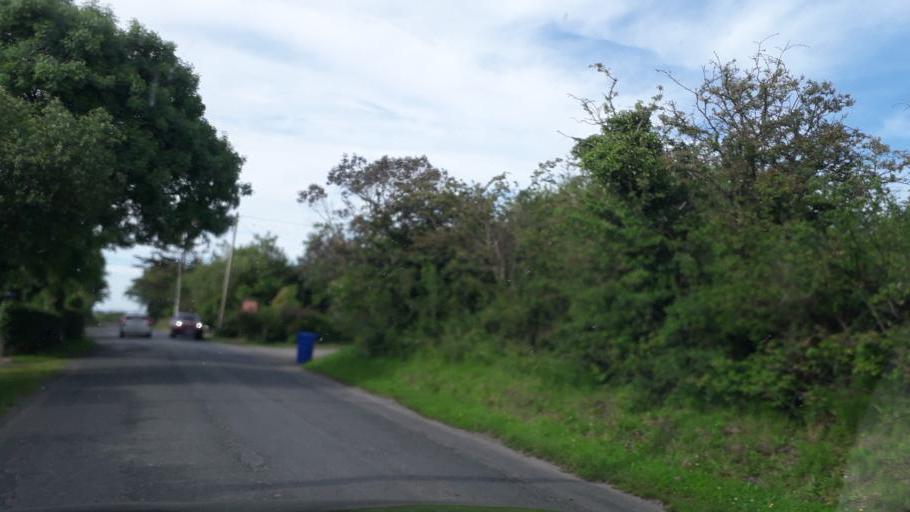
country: IE
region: Leinster
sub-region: Loch Garman
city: Courtown
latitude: 52.5831
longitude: -6.2310
